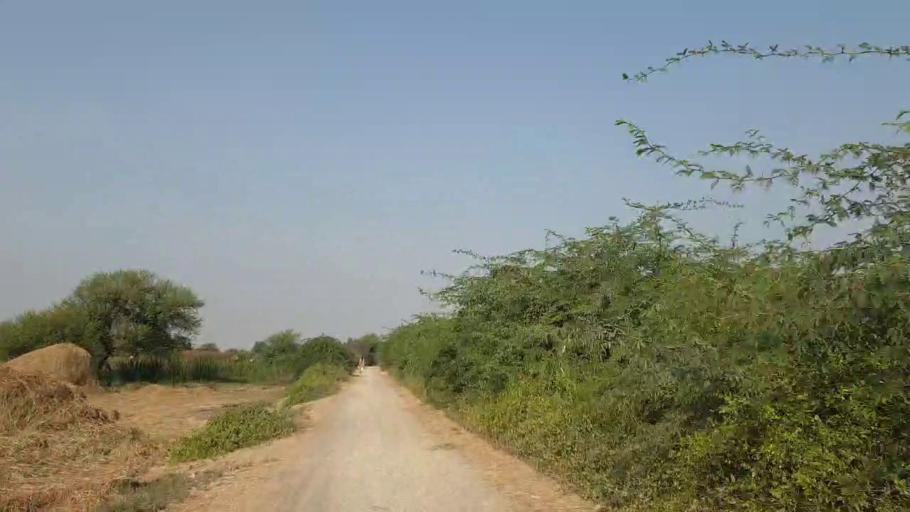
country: PK
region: Sindh
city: Matli
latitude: 24.9490
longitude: 68.5565
